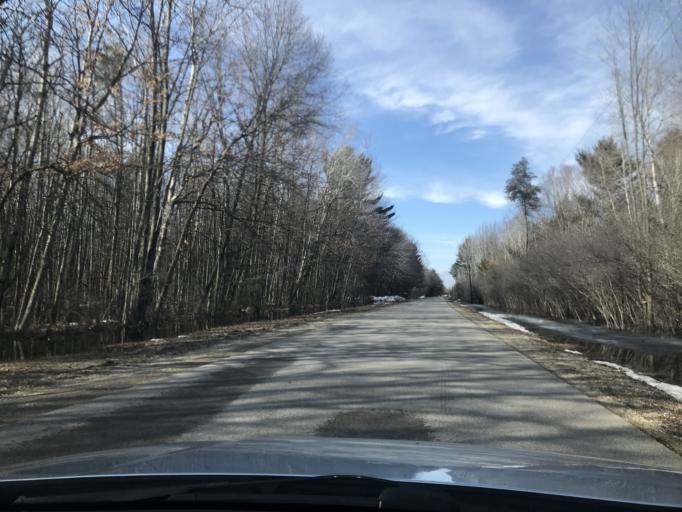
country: US
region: Wisconsin
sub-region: Marinette County
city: Marinette
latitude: 45.0315
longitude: -87.6676
